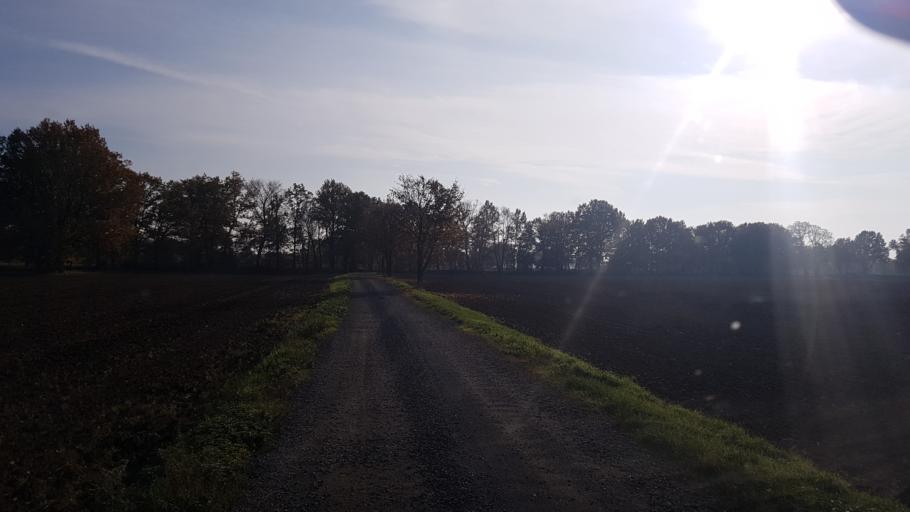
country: DE
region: Brandenburg
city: Falkenberg
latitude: 51.6185
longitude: 13.2983
